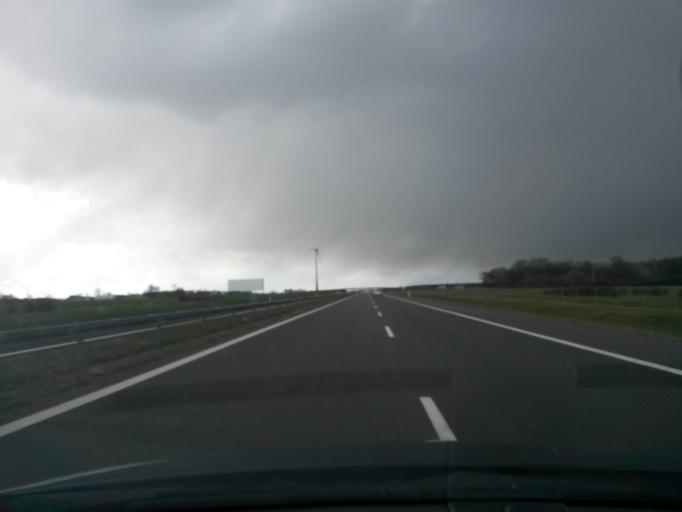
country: PL
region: Greater Poland Voivodeship
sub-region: Powiat sredzki
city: Dominowo
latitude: 52.3101
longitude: 17.2875
